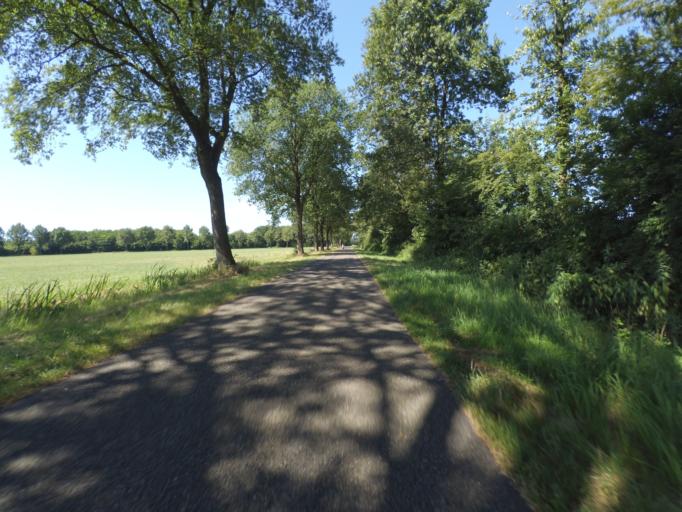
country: NL
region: Drenthe
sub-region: Gemeente Aa en Hunze
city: Anloo
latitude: 52.9297
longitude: 6.6656
